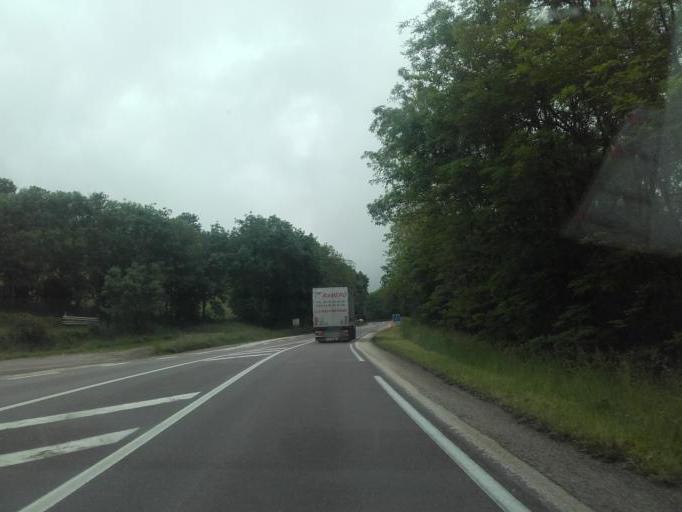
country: FR
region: Bourgogne
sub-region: Departement de la Cote-d'Or
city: Nolay
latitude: 46.9571
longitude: 4.6713
